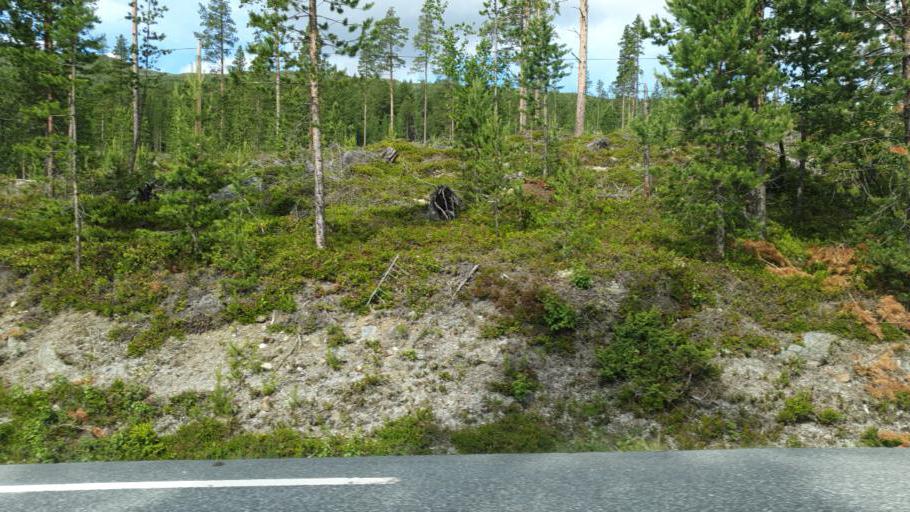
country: NO
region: Oppland
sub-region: Vaga
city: Vagamo
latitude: 61.7339
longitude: 9.0898
